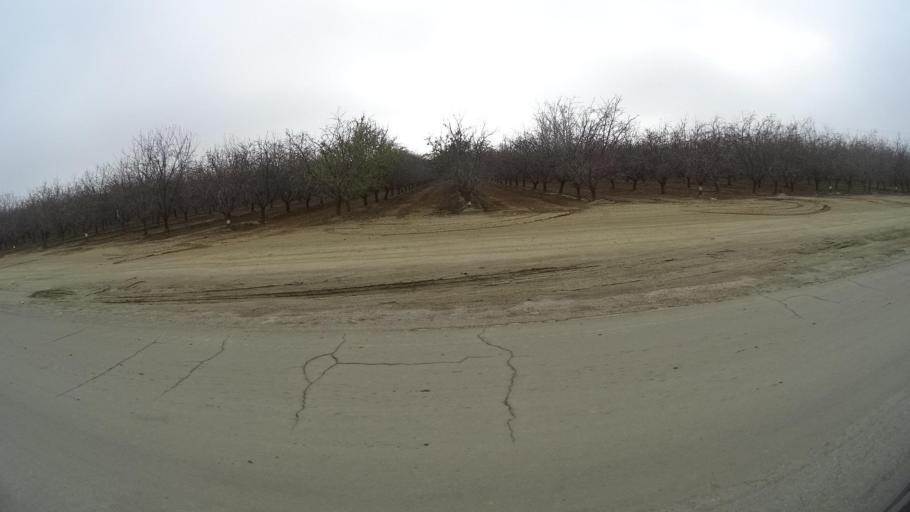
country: US
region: California
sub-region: Kern County
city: Maricopa
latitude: 35.0938
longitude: -119.2329
